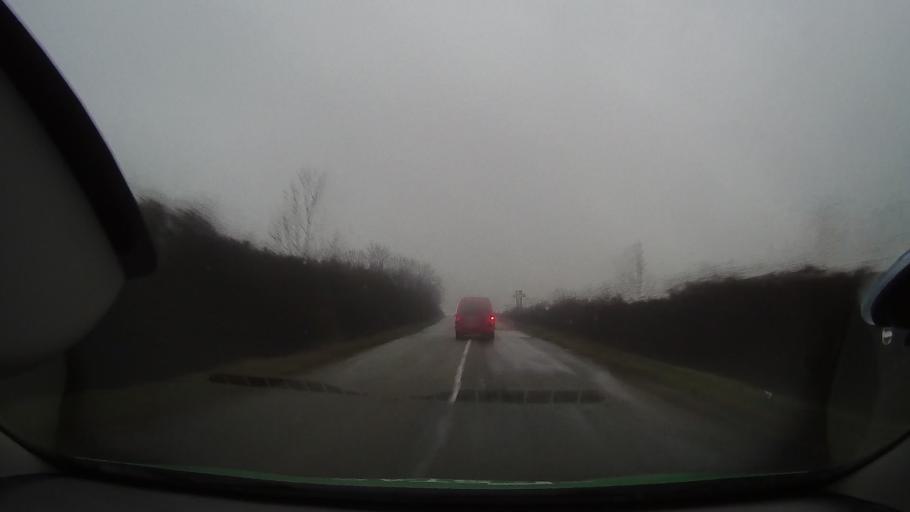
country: RO
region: Arad
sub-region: Comuna Craiova
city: Craiova
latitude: 46.6163
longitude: 21.9573
